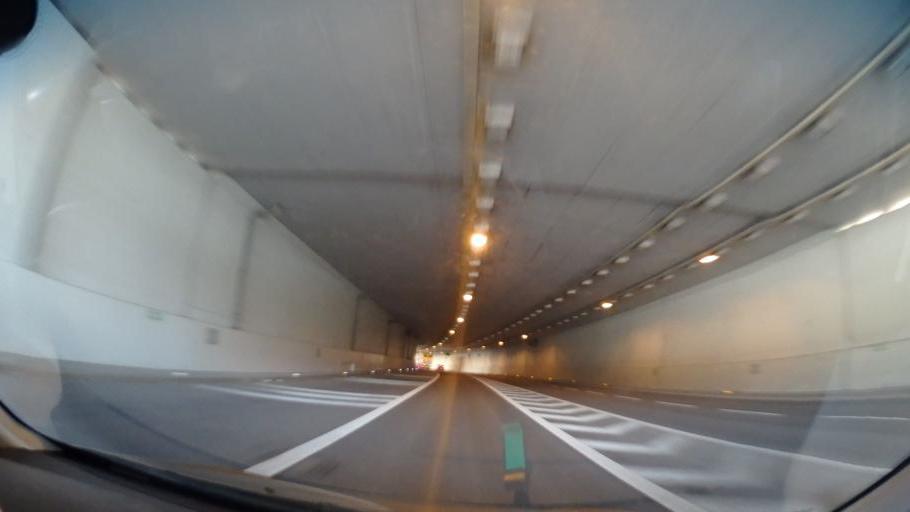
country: CZ
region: South Moravian
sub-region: Mesto Brno
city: Brno
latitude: 49.1913
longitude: 16.5697
